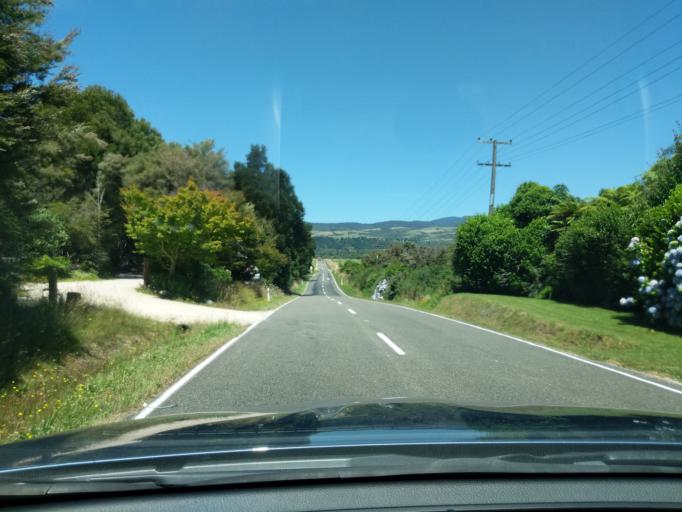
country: NZ
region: Tasman
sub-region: Tasman District
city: Takaka
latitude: -40.7268
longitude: 172.6073
